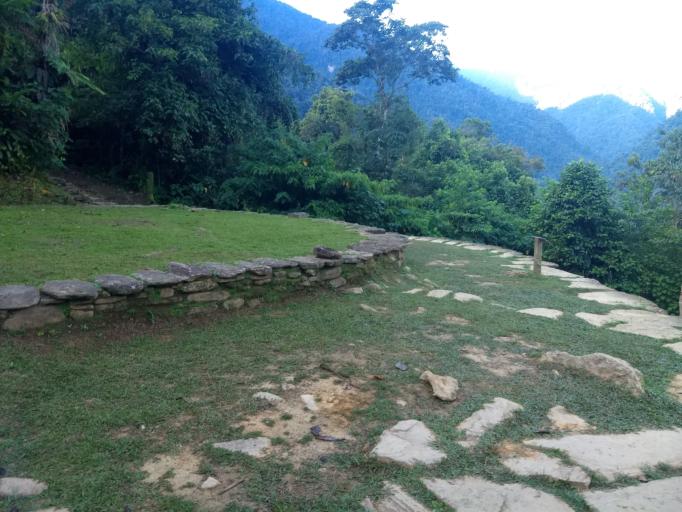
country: CO
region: Magdalena
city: Cienaga
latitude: 11.0414
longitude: -73.9243
